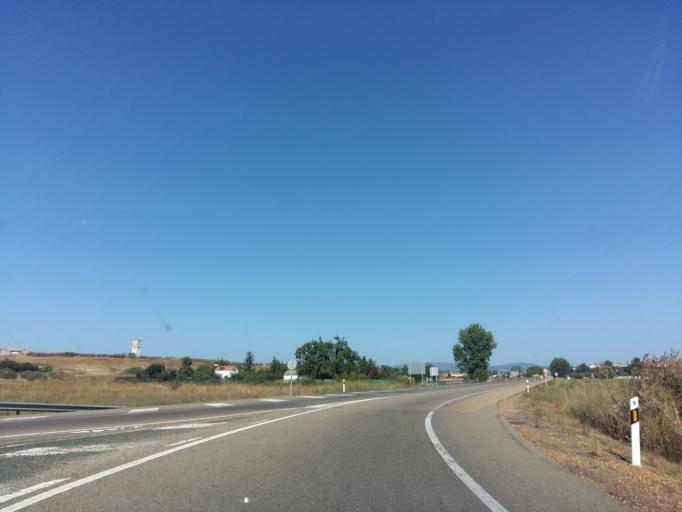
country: ES
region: Castille and Leon
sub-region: Provincia de Leon
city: Astorga
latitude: 42.4410
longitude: -6.0388
